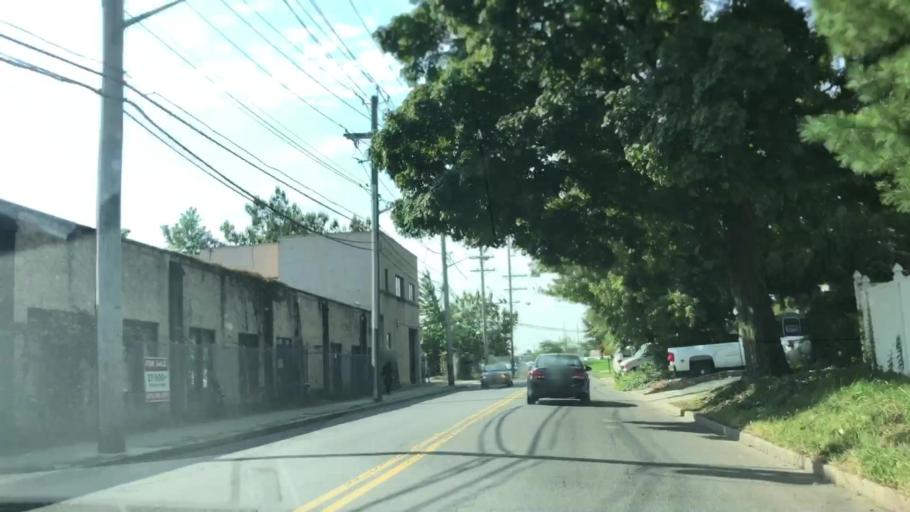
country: US
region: New Jersey
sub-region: Essex County
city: Bloomfield
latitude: 40.7830
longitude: -74.1860
